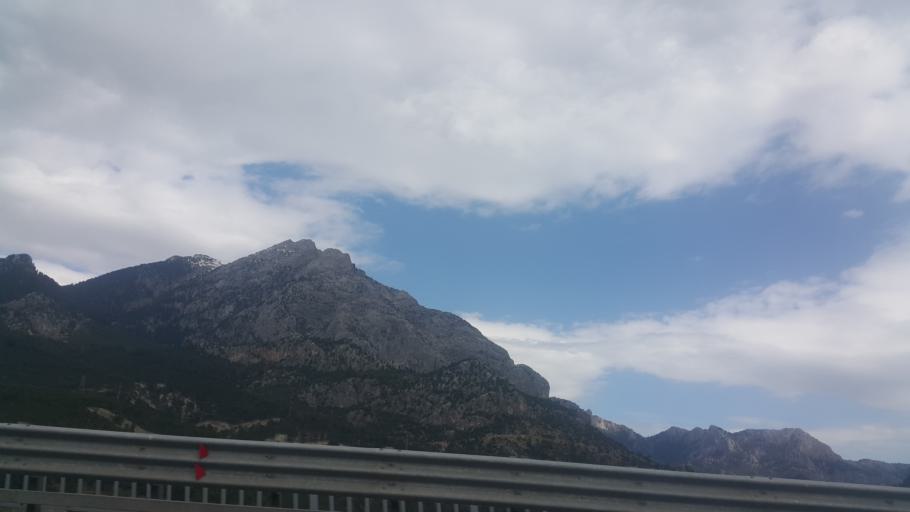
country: TR
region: Adana
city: Pozanti
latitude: 37.4094
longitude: 34.8824
